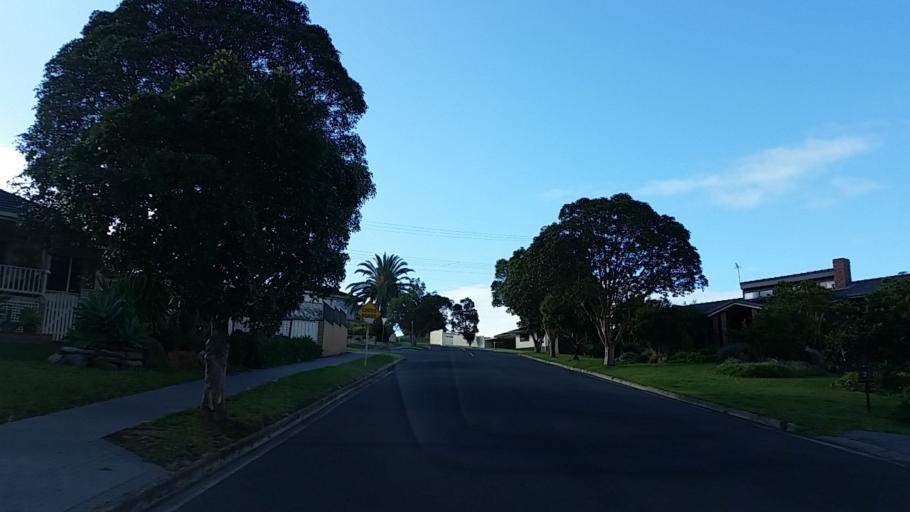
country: AU
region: South Australia
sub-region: Marion
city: Clovelly Park
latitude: -35.0074
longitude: 138.5879
